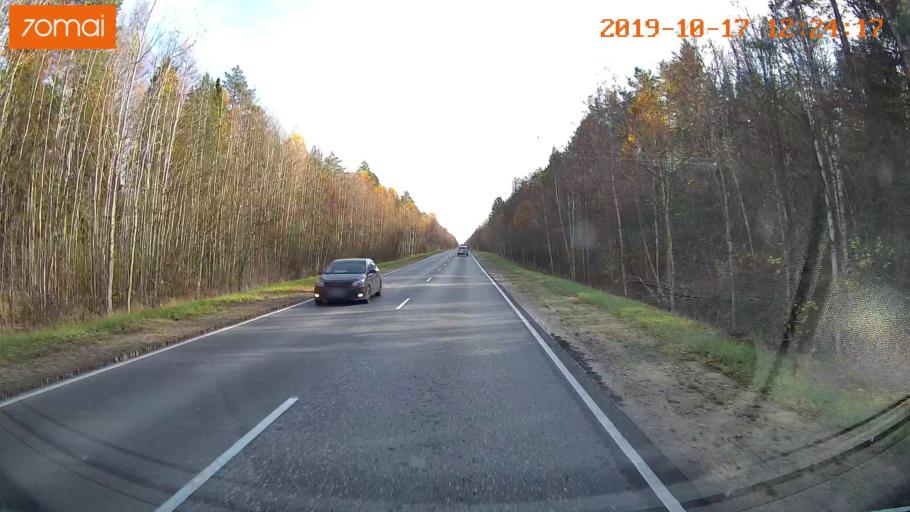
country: RU
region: Rjazan
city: Gus'-Zheleznyy
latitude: 55.0368
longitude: 41.2117
